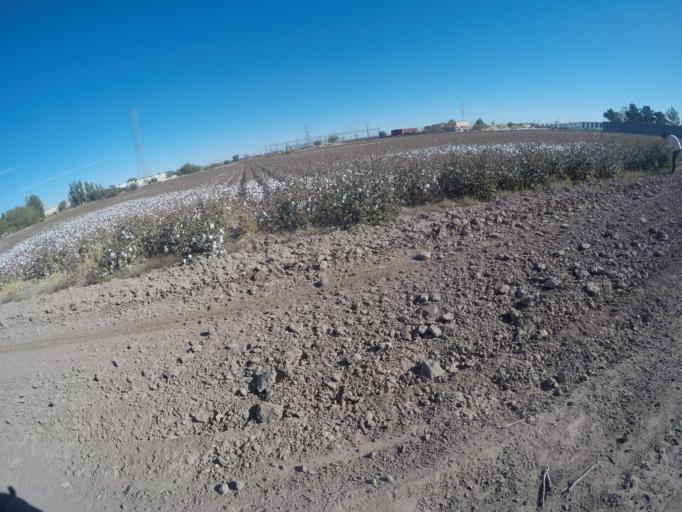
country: US
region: Texas
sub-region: El Paso County
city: Socorro
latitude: 31.6982
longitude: -106.3762
